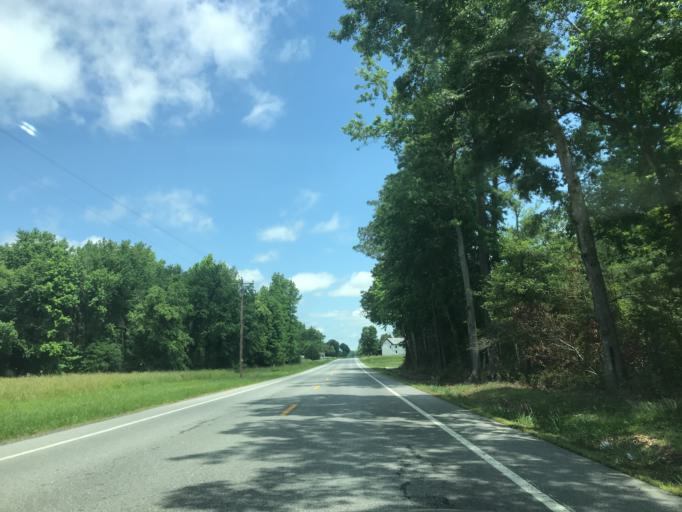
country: US
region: Maryland
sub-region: Caroline County
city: Federalsburg
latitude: 38.7145
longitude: -75.7427
